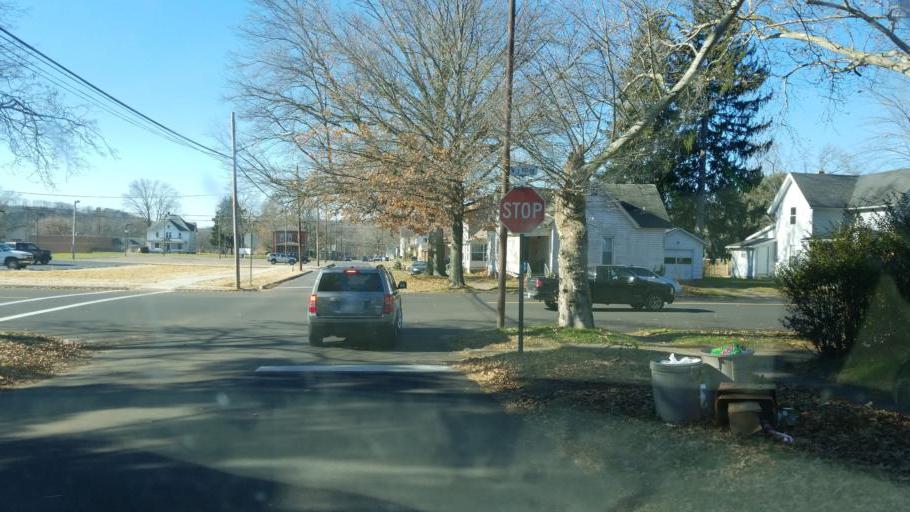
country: US
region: Ohio
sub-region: Coshocton County
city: Coshocton
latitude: 40.2764
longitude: -81.8666
